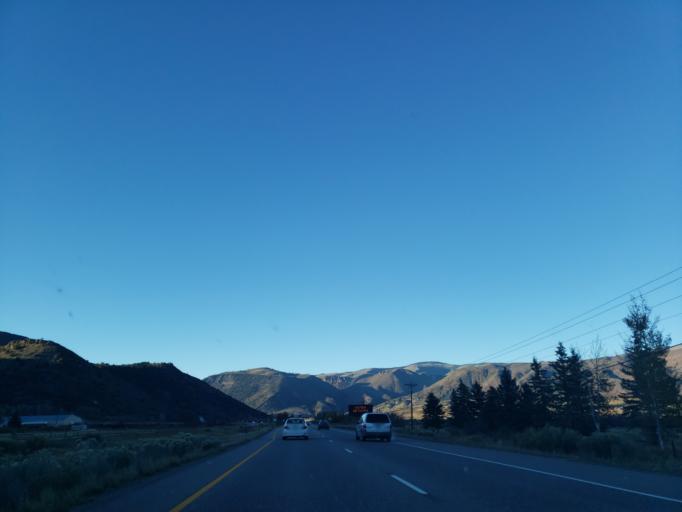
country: US
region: Colorado
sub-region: Pitkin County
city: Snowmass Village
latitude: 39.2554
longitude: -106.8857
